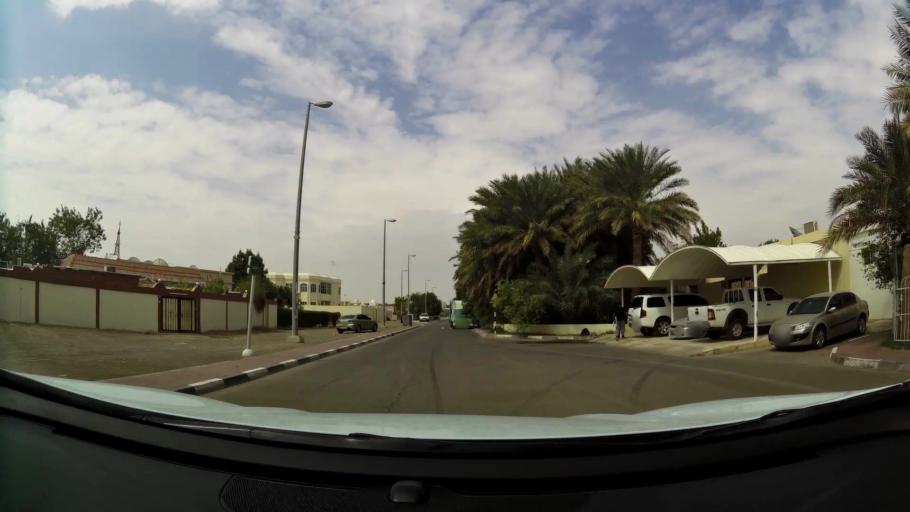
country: AE
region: Abu Dhabi
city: Al Ain
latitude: 24.1973
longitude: 55.7899
